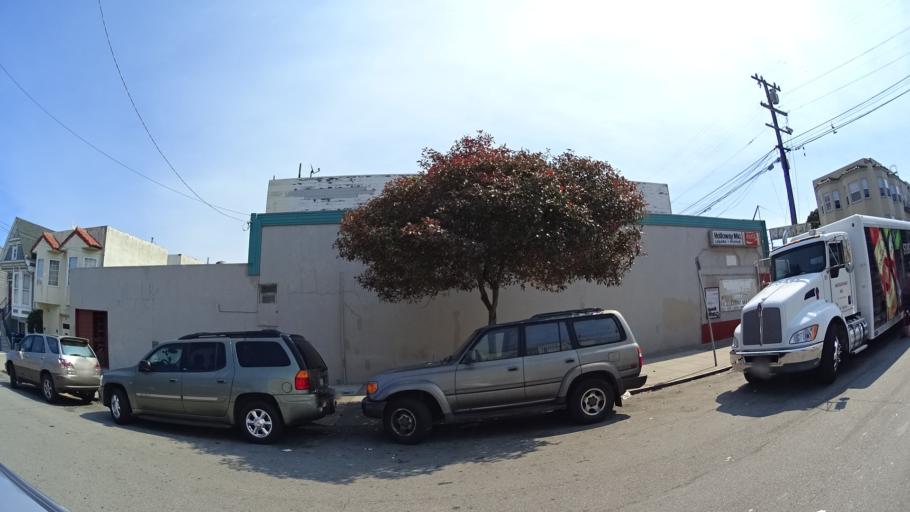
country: US
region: California
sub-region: San Mateo County
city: Daly City
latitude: 37.7222
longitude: -122.4551
